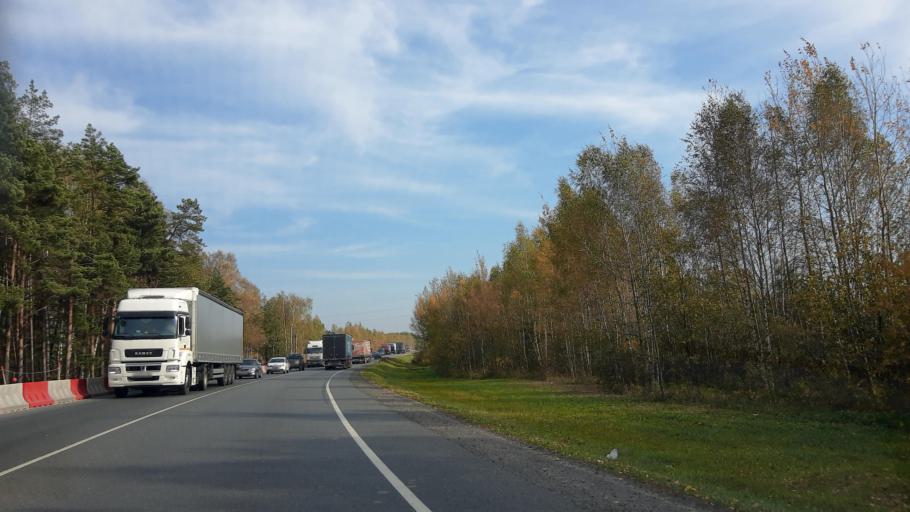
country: RU
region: Moskovskaya
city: Fryazevo
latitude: 55.7341
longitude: 38.4322
